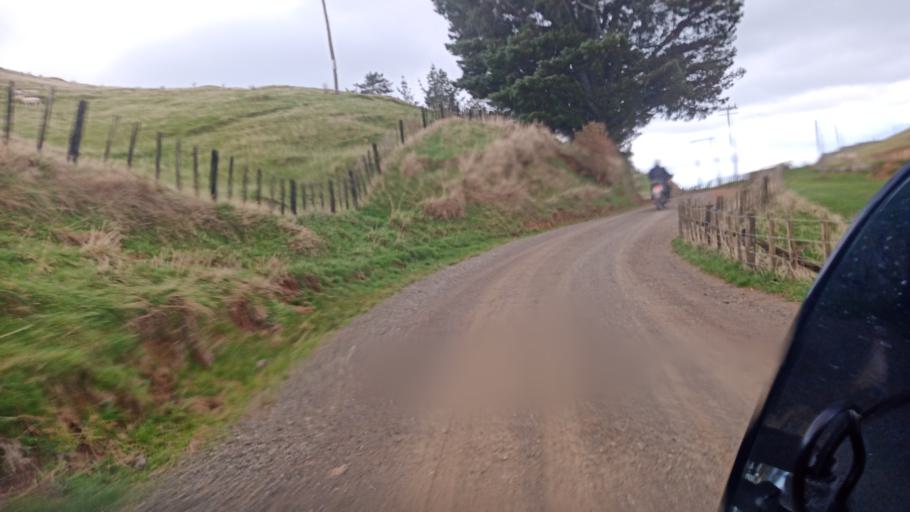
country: NZ
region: Gisborne
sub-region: Gisborne District
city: Gisborne
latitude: -38.4842
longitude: 177.6066
